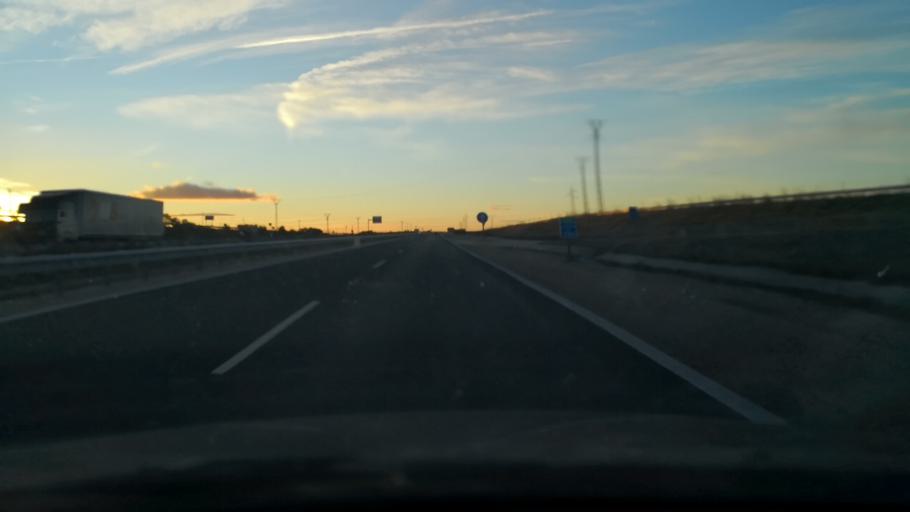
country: ES
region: Castille and Leon
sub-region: Provincia de Valladolid
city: Tordesillas
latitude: 41.5047
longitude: -5.0436
